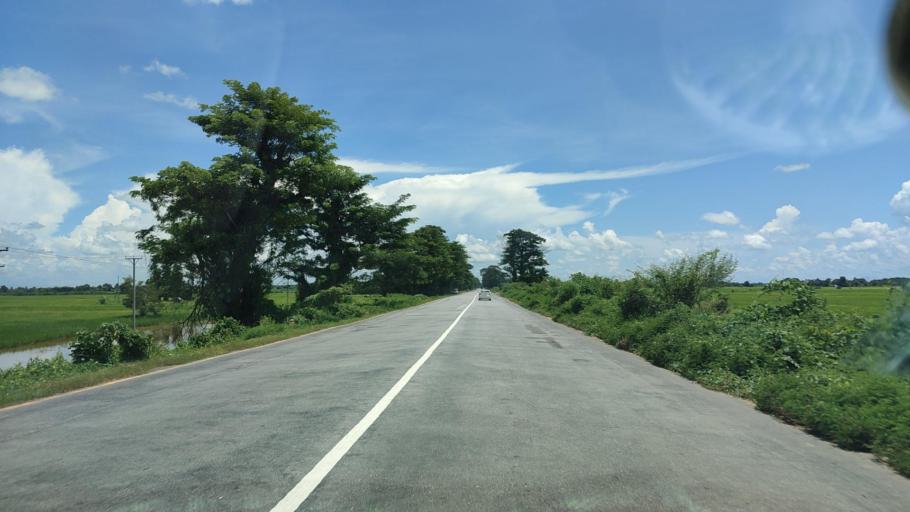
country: MM
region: Bago
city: Pyu
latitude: 18.2992
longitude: 96.5107
